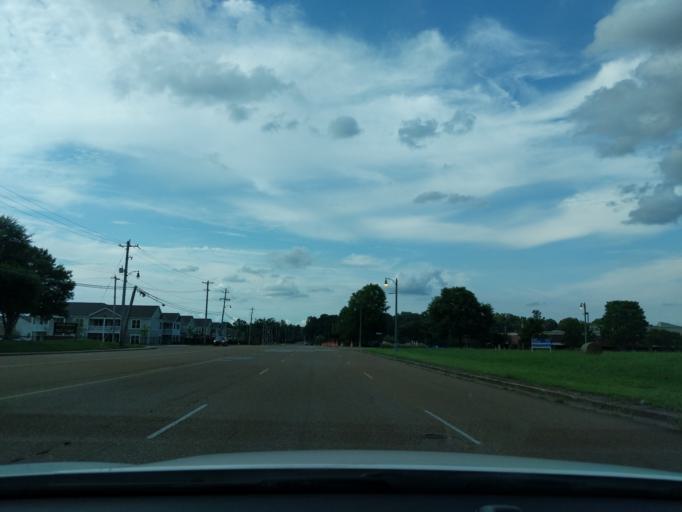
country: US
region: Tennessee
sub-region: Shelby County
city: Germantown
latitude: 35.0436
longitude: -89.7597
